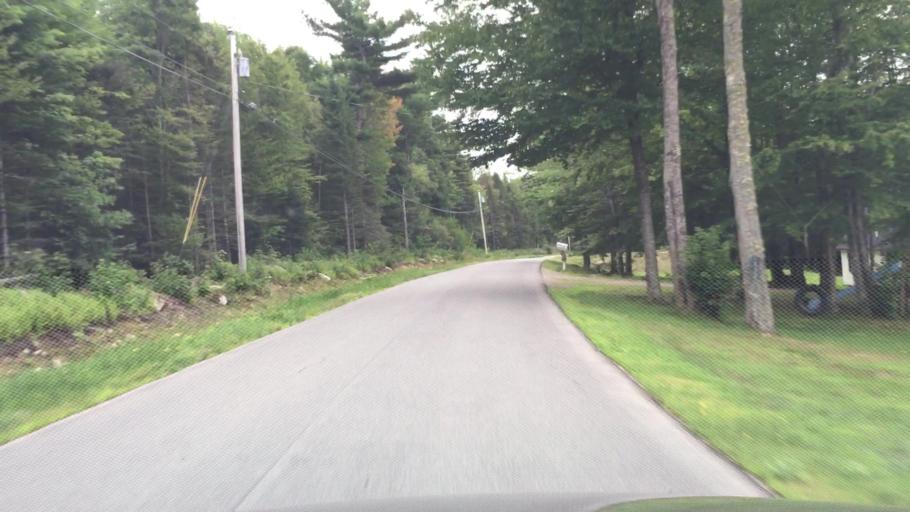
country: US
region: Maine
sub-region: Waldo County
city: Stockton Springs
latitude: 44.5148
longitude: -68.8754
